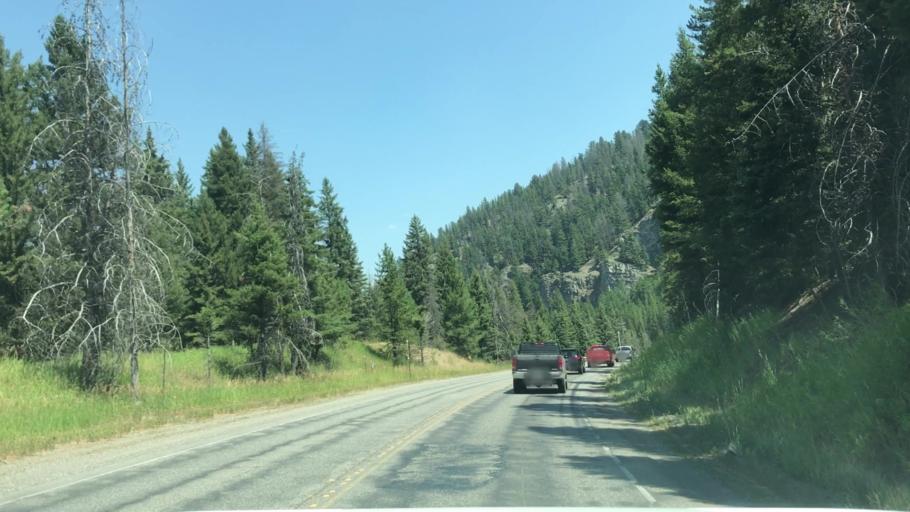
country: US
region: Montana
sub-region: Gallatin County
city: Big Sky
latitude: 45.2877
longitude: -111.2208
